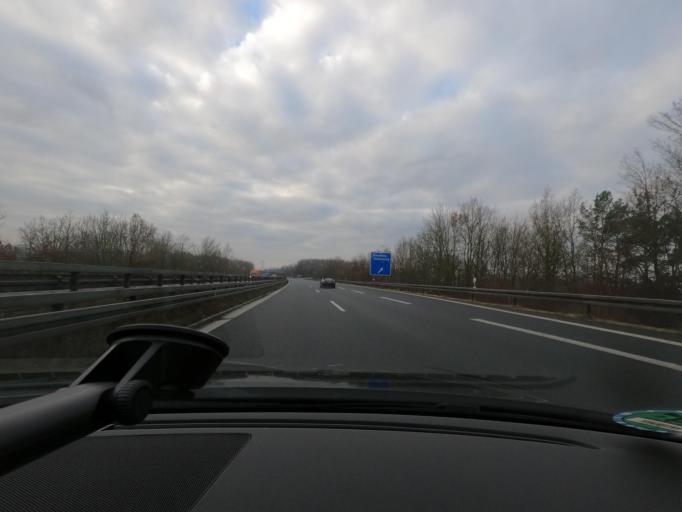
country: DE
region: Bavaria
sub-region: Upper Franconia
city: Ebensfeld
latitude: 50.0620
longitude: 10.9700
